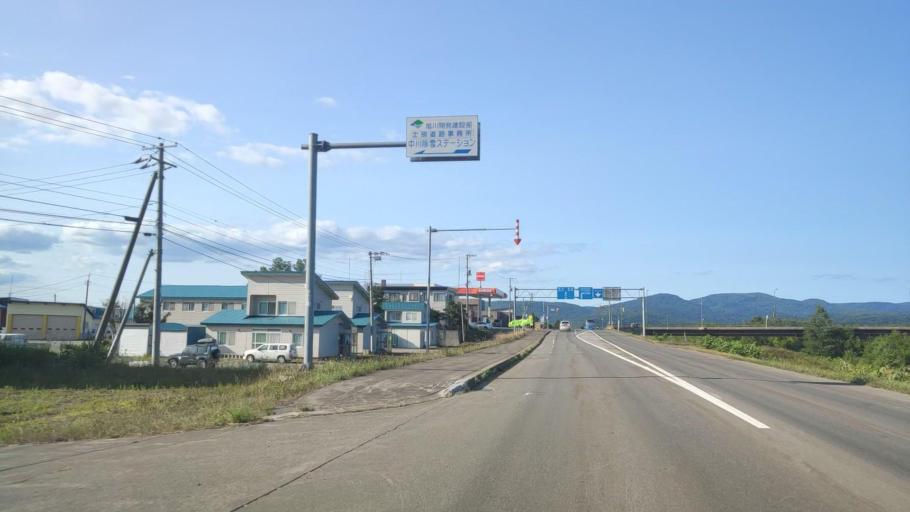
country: JP
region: Hokkaido
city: Makubetsu
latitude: 44.8170
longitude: 142.0671
